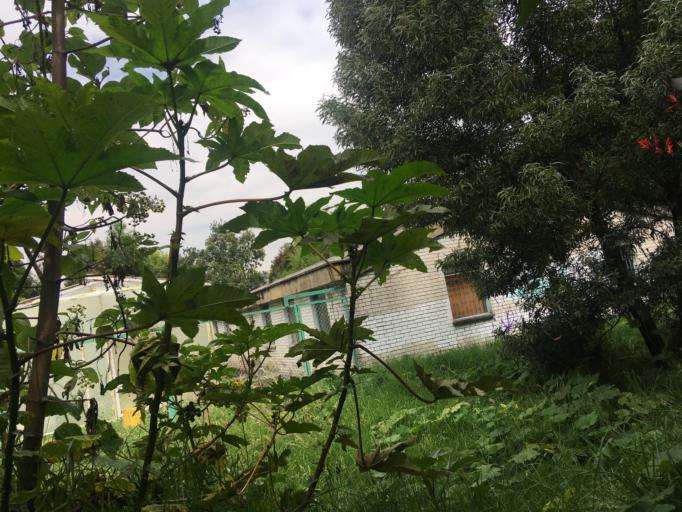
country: CO
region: Bogota D.C.
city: Bogota
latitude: 4.6414
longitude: -74.0814
